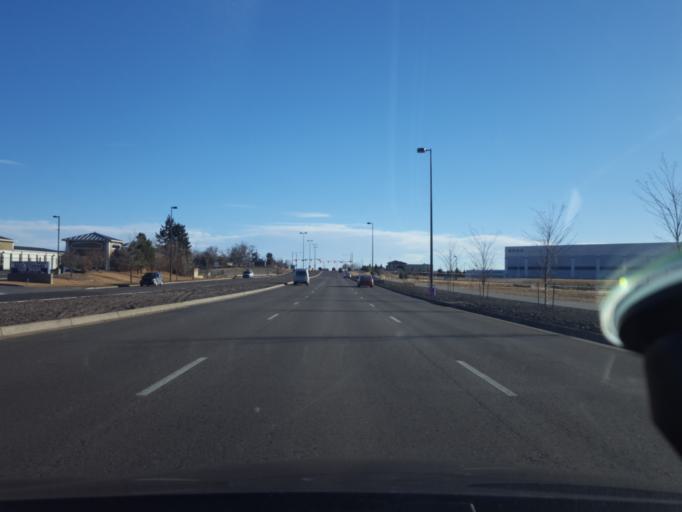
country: US
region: Colorado
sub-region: Adams County
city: Aurora
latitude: 39.7732
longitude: -104.7723
